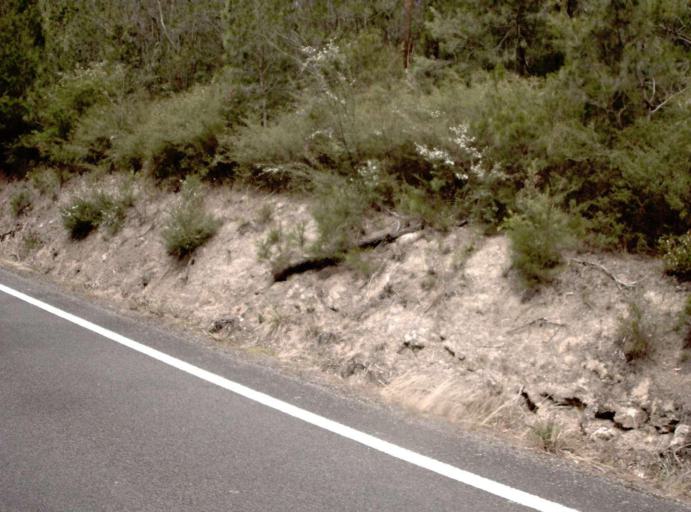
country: AU
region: New South Wales
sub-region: Bega Valley
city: Eden
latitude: -37.4971
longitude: 149.5465
